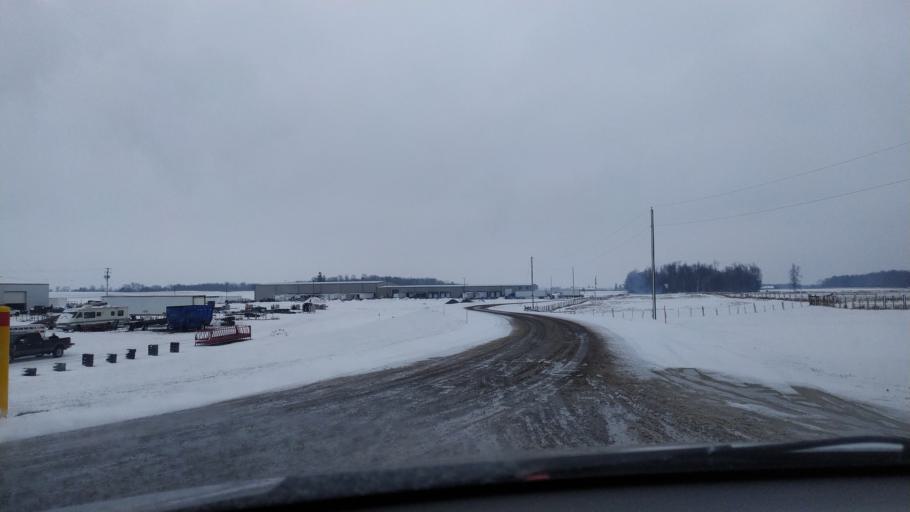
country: CA
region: Ontario
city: Waterloo
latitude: 43.5945
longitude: -80.6213
